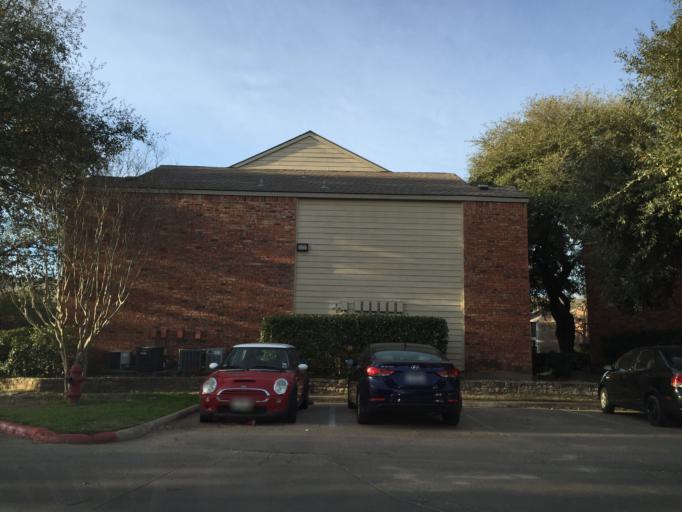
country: US
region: Texas
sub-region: Williamson County
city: Jollyville
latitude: 30.4123
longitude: -97.7440
